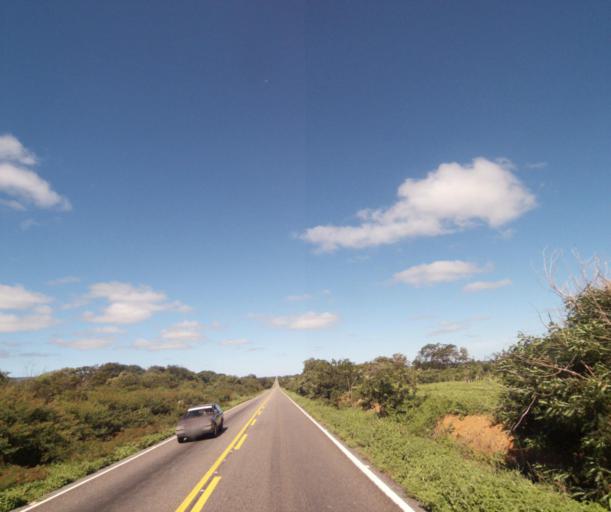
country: BR
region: Bahia
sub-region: Palmas De Monte Alto
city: Palmas de Monte Alto
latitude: -14.2380
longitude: -43.0180
